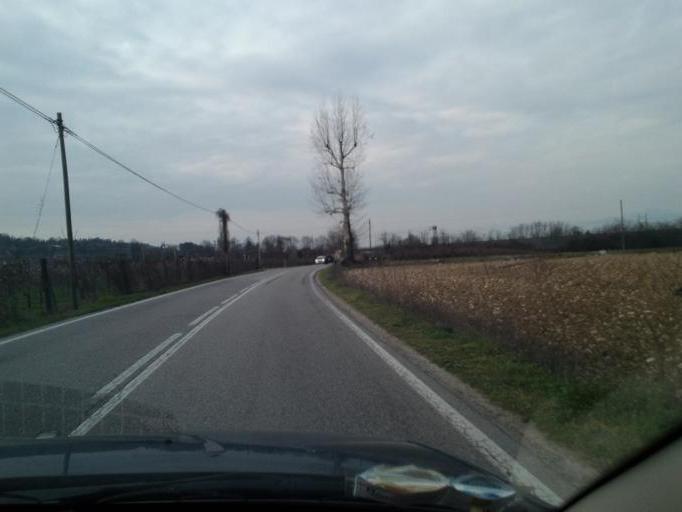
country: IT
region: Veneto
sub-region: Provincia di Verona
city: Sona
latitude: 45.4247
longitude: 10.8486
